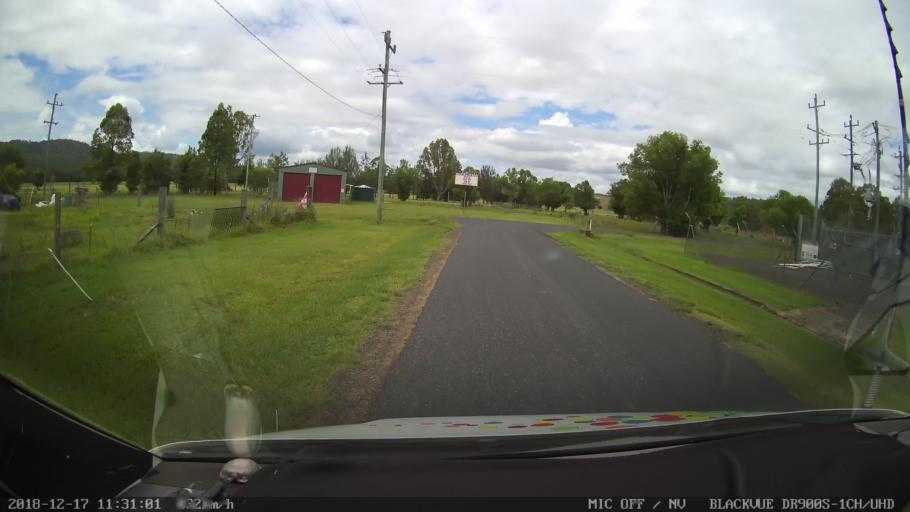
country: AU
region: New South Wales
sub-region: Kyogle
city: Kyogle
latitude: -28.7384
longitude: 152.6220
